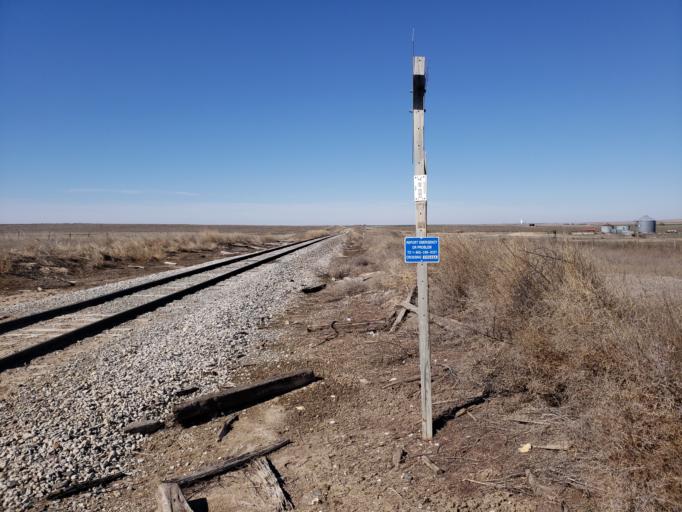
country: US
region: Kansas
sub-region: Ness County
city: Ness City
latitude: 38.4481
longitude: -99.9906
